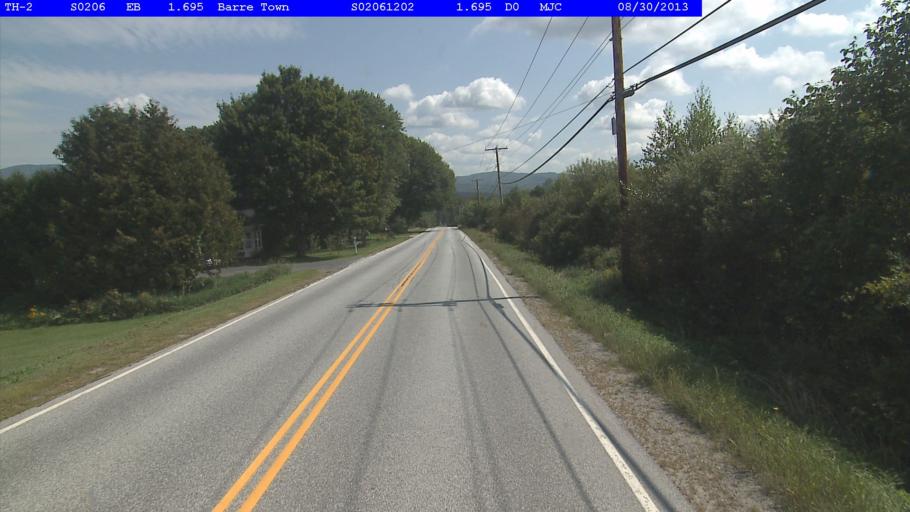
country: US
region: Vermont
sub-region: Washington County
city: South Barre
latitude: 44.1607
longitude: -72.4632
